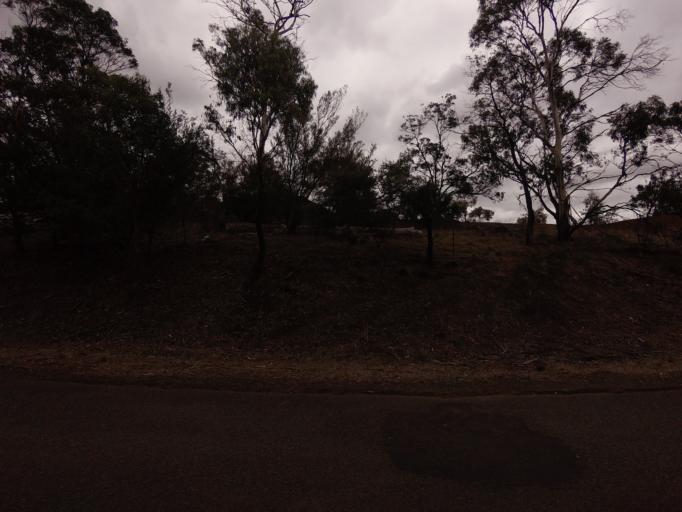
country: AU
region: Tasmania
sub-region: Clarence
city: Cambridge
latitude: -42.7920
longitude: 147.4015
